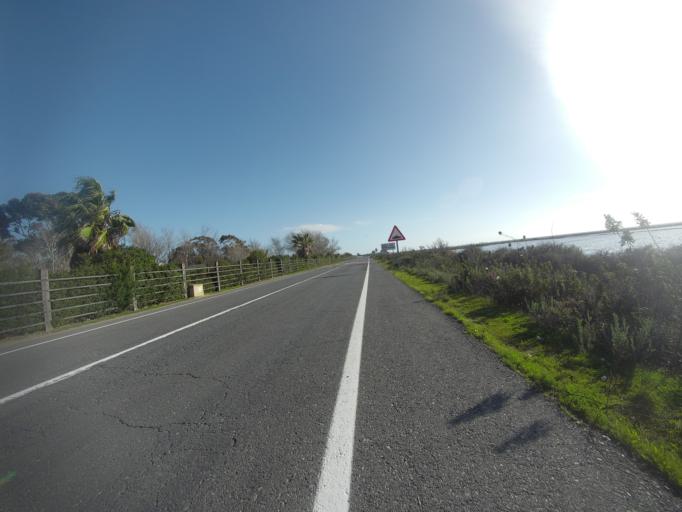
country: ES
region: Andalusia
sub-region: Provincia de Huelva
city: Huelva
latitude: 37.2531
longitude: -6.9693
